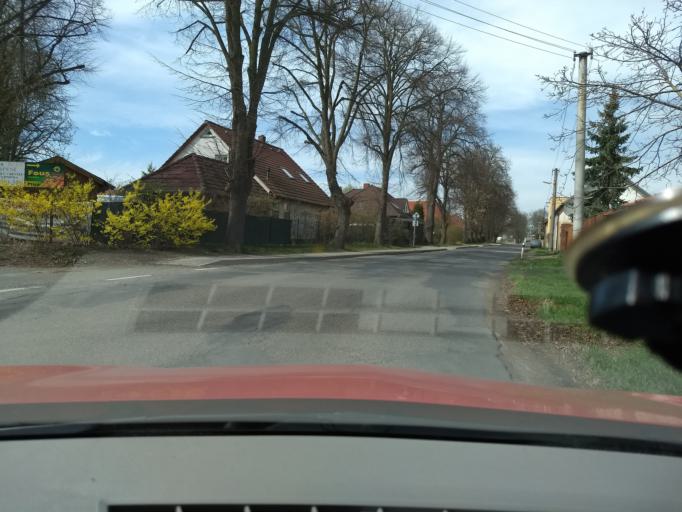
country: CZ
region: Central Bohemia
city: Jenec
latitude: 50.0462
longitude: 14.1828
